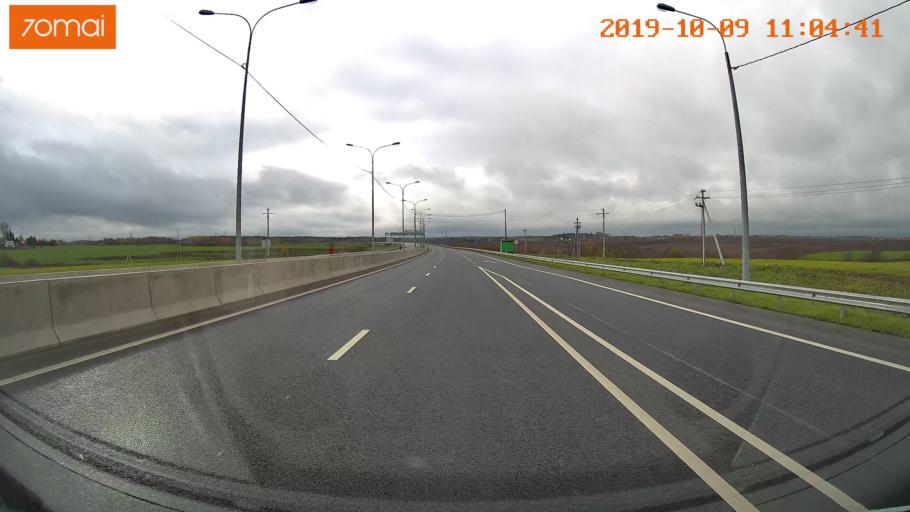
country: RU
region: Vologda
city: Molochnoye
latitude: 59.2095
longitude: 39.7650
